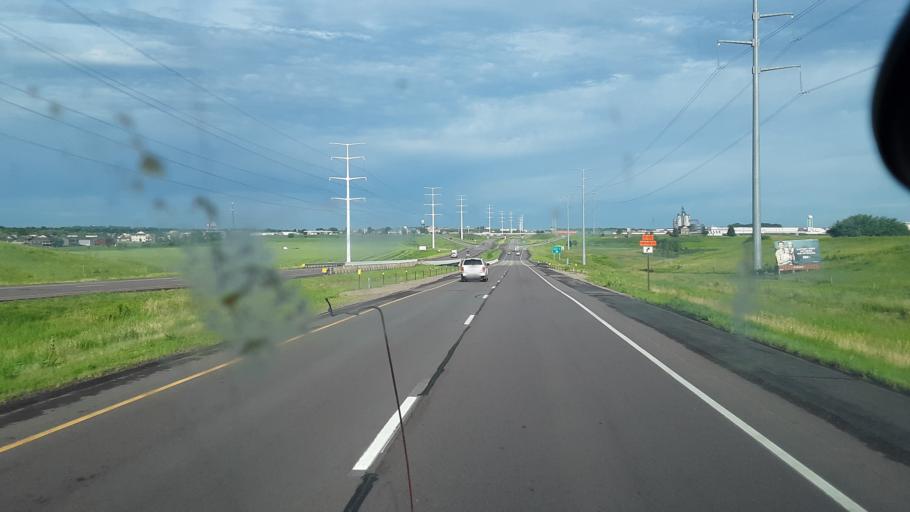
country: US
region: South Dakota
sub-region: Minnehaha County
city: Brandon
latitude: 43.6086
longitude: -96.5607
